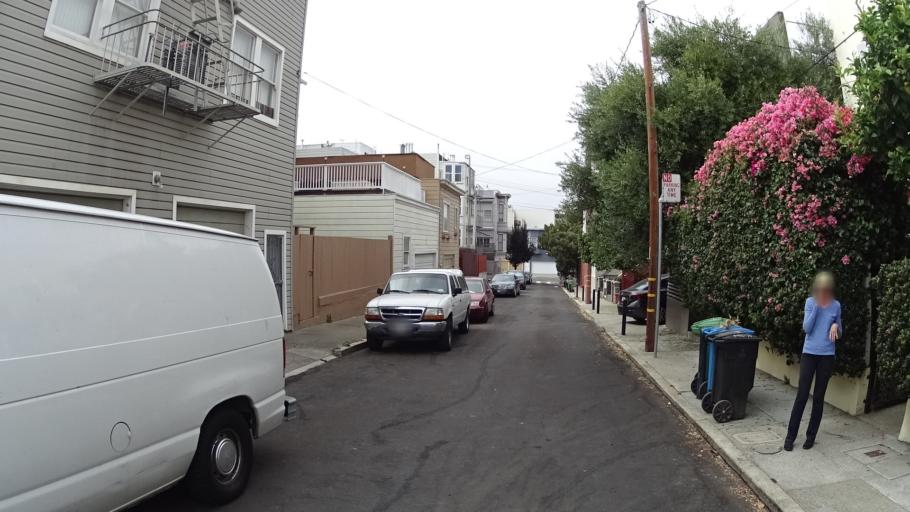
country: US
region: California
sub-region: San Francisco County
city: San Francisco
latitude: 37.7992
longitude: -122.4299
